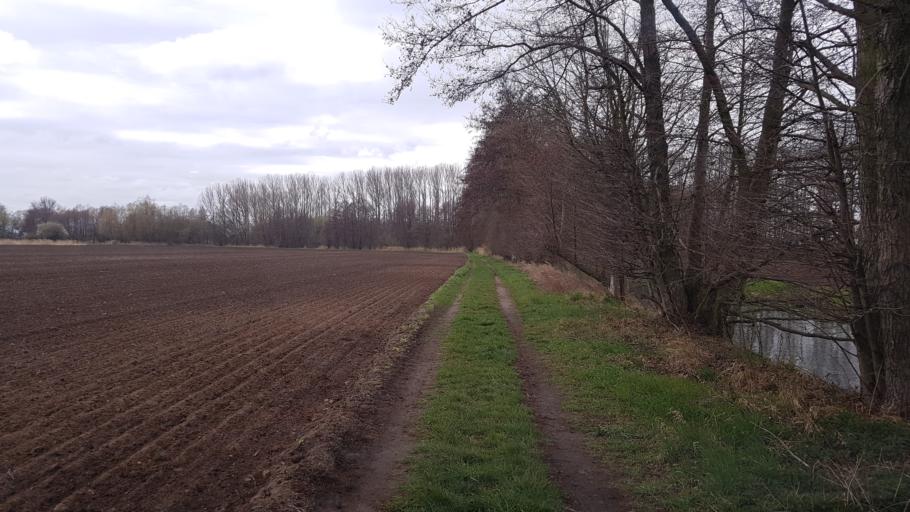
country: DE
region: Brandenburg
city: Doberlug-Kirchhain
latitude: 51.6502
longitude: 13.5599
